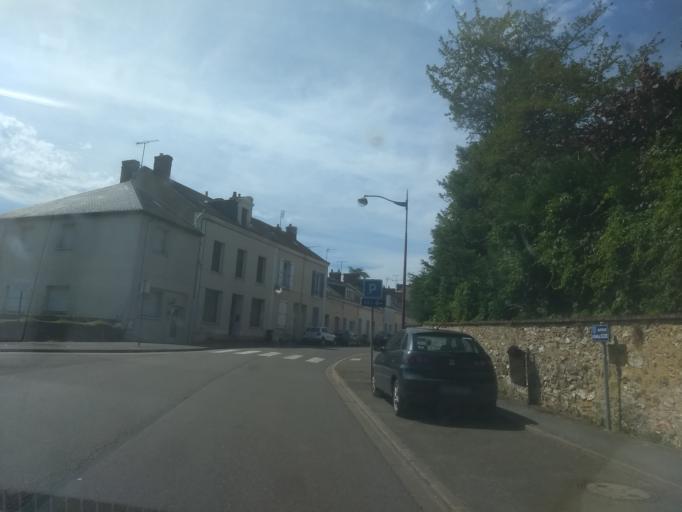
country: FR
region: Centre
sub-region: Departement d'Eure-et-Loir
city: Nogent-le-Rotrou
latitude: 48.3250
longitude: 0.8074
